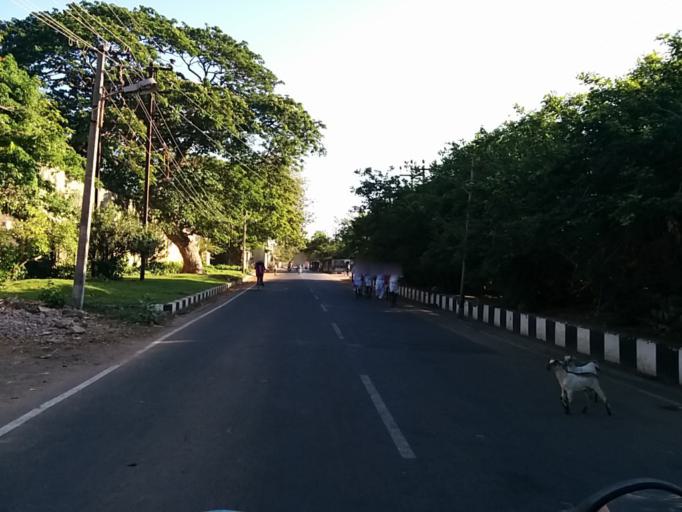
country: IN
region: Pondicherry
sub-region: Puducherry
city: Puducherry
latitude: 11.9207
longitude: 79.8302
